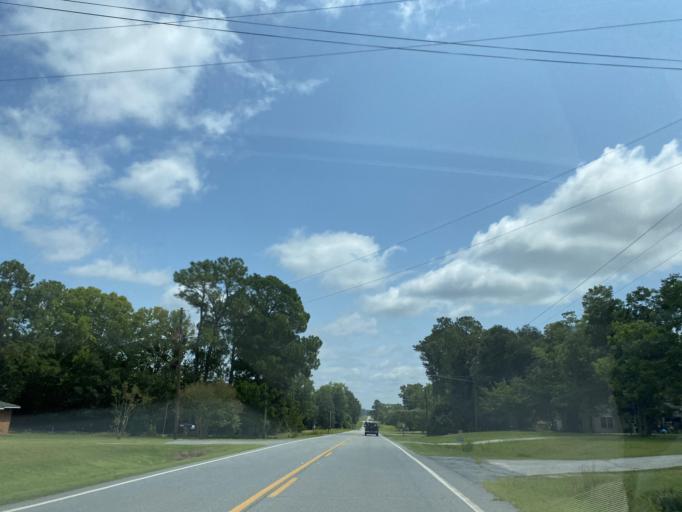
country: US
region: Georgia
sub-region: Telfair County
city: Helena
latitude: 32.0183
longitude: -83.0529
